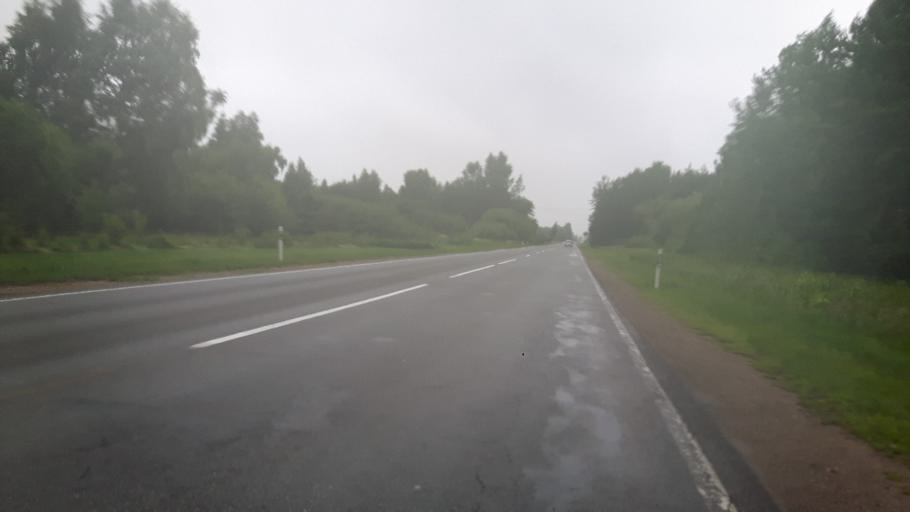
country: LV
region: Liepaja
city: Liepaja
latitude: 56.4274
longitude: 21.0074
